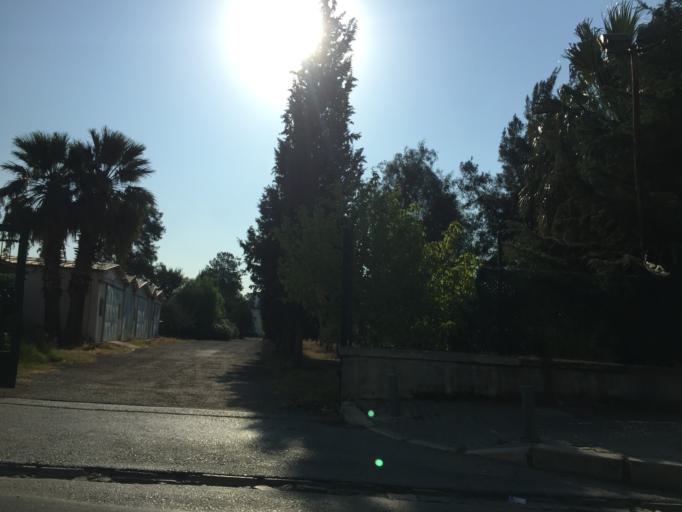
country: TR
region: Izmir
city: Buca
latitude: 38.4440
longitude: 27.1804
